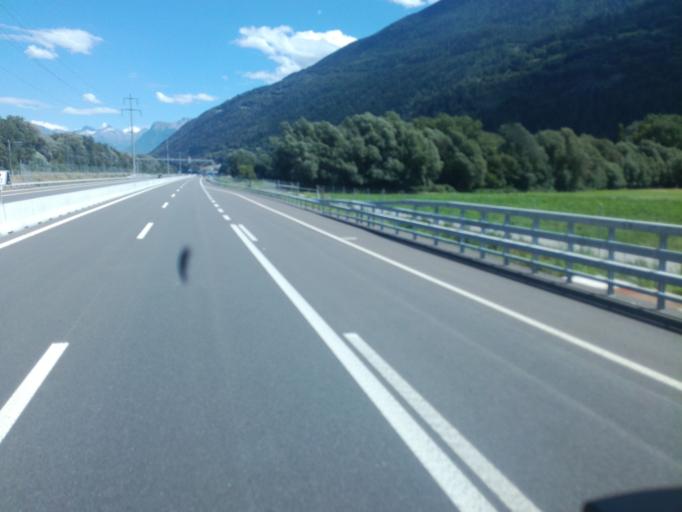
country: CH
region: Valais
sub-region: Leuk District
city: Turtmann
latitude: 46.3089
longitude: 7.7149
